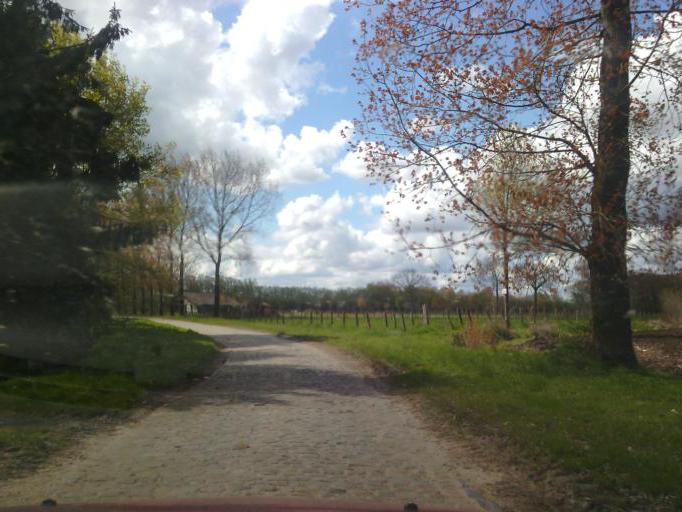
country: BE
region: Flanders
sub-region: Provincie Oost-Vlaanderen
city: Lokeren
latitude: 51.0768
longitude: 3.9430
